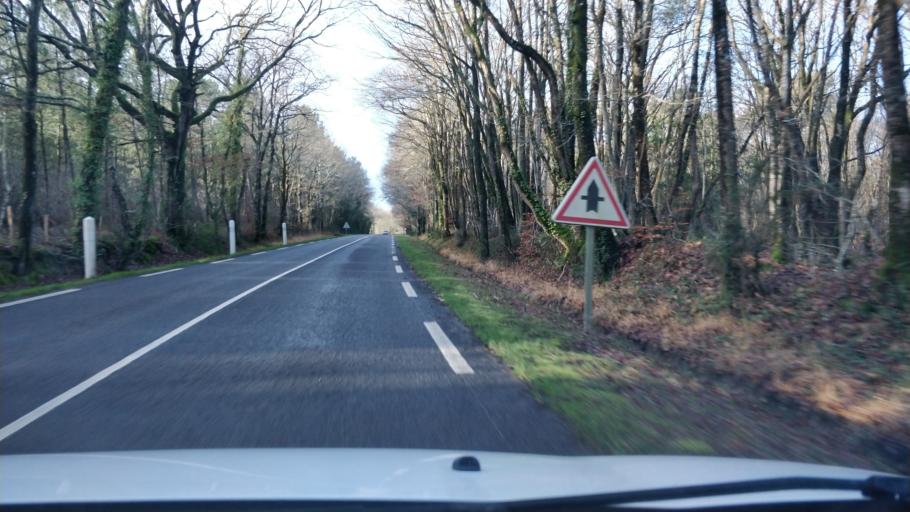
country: FR
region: Pays de la Loire
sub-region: Departement de la Loire-Atlantique
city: Herbignac
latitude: 47.4356
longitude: -2.3424
